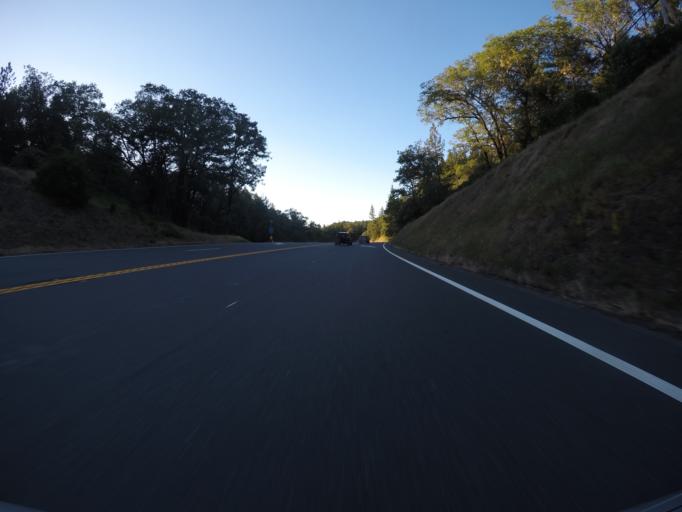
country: US
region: California
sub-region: Mendocino County
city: Laytonville
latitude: 39.7551
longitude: -123.5369
